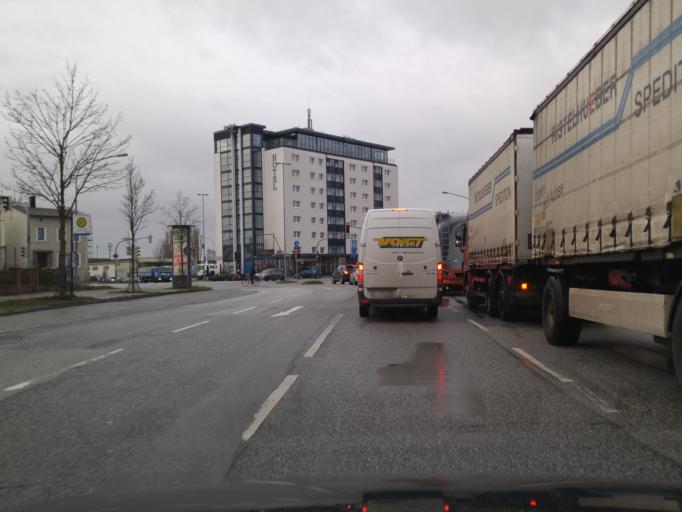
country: DE
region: Schleswig-Holstein
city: Luebeck
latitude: 53.8799
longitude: 10.6790
